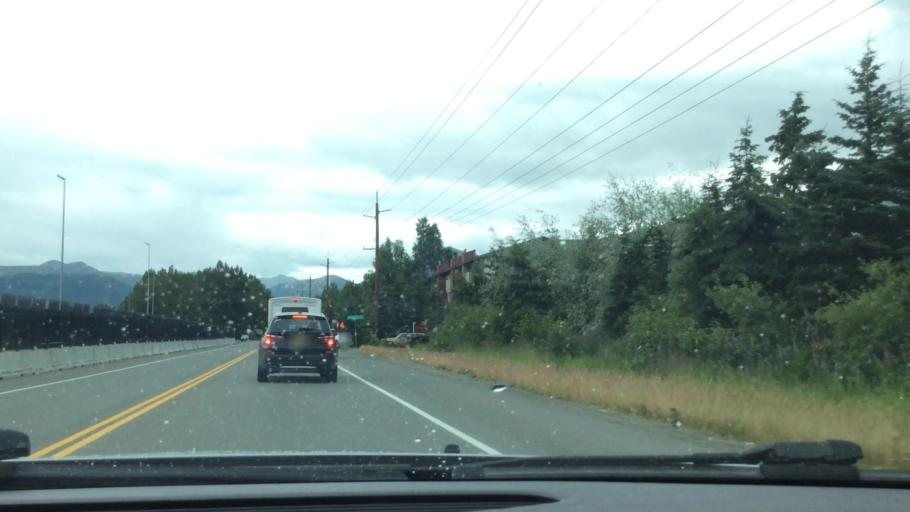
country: US
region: Alaska
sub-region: Anchorage Municipality
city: Elmendorf Air Force Base
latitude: 61.2242
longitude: -149.7500
